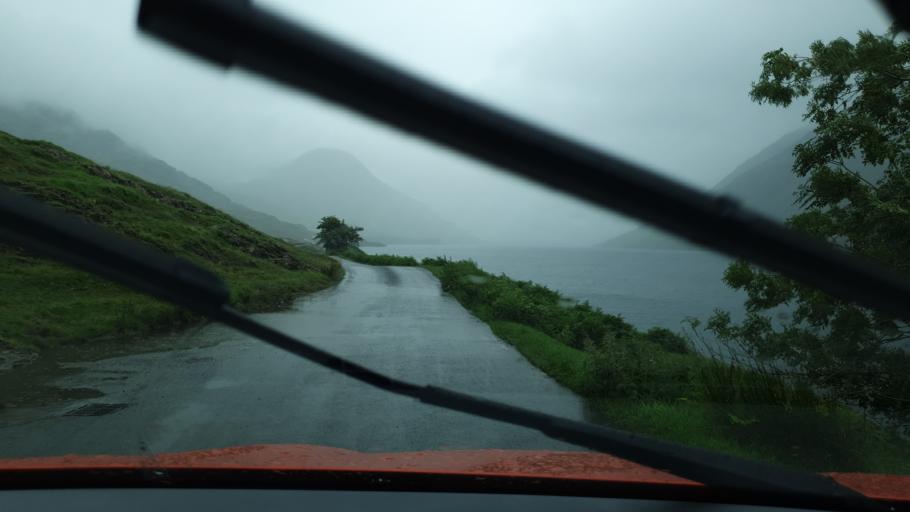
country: GB
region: England
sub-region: Cumbria
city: Seascale
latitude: 54.4317
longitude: -3.3149
